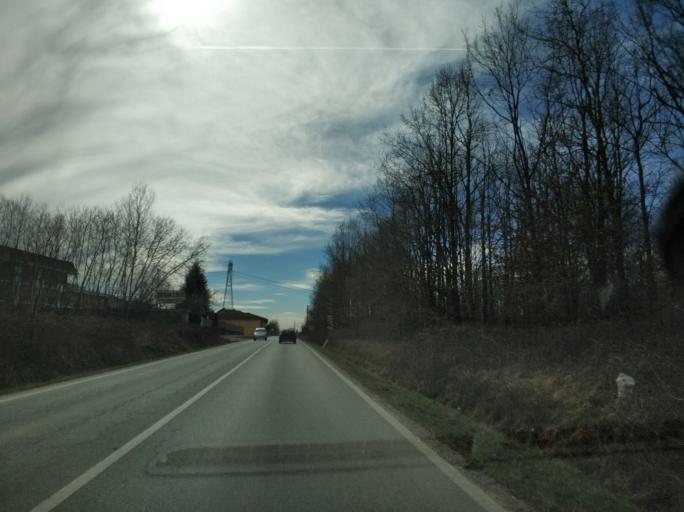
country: IT
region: Piedmont
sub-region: Provincia di Torino
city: Lombardore
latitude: 45.2174
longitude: 7.7305
